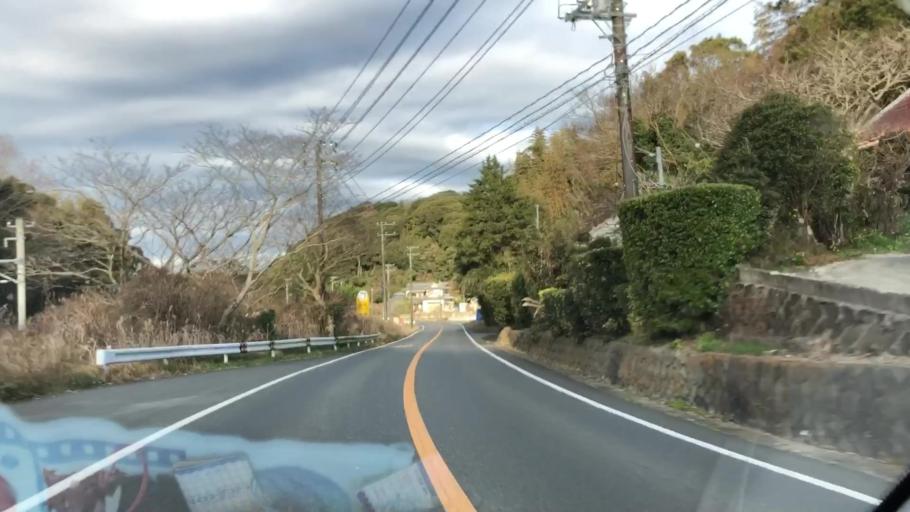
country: JP
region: Chiba
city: Tateyama
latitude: 34.9892
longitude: 139.9279
